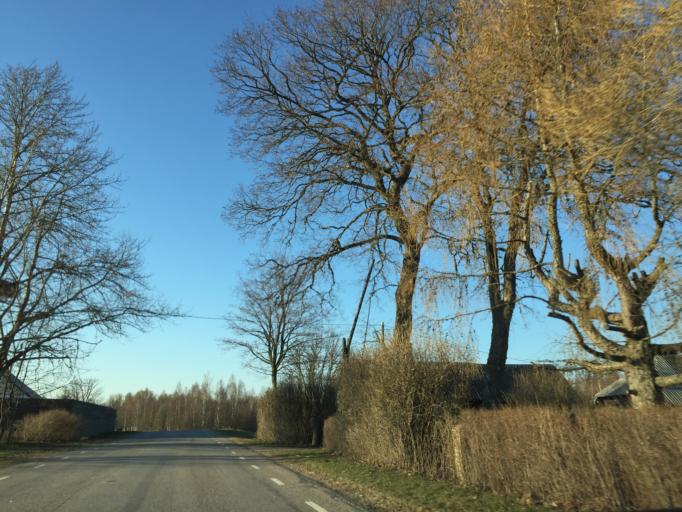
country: EE
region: Ida-Virumaa
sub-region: Toila vald
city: Voka
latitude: 59.1858
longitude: 27.5618
